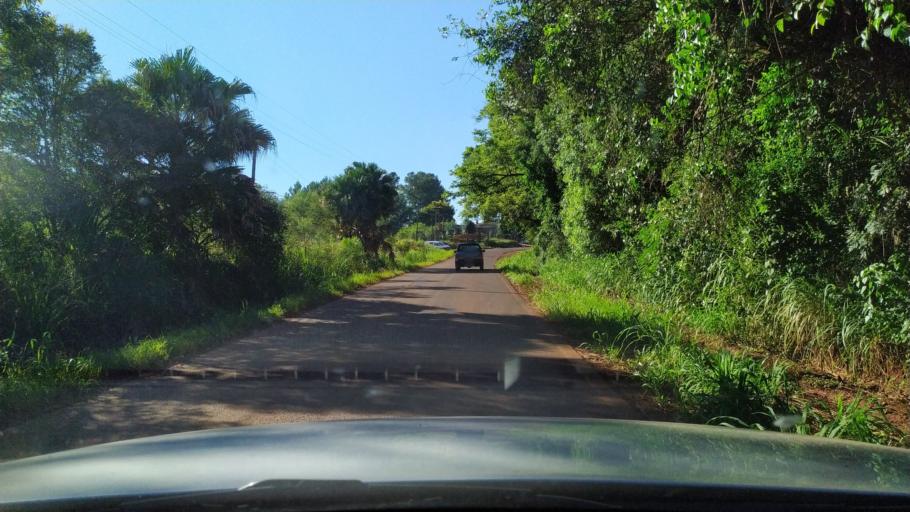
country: AR
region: Misiones
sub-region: Departamento de Montecarlo
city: Montecarlo
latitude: -26.5995
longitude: -54.7028
